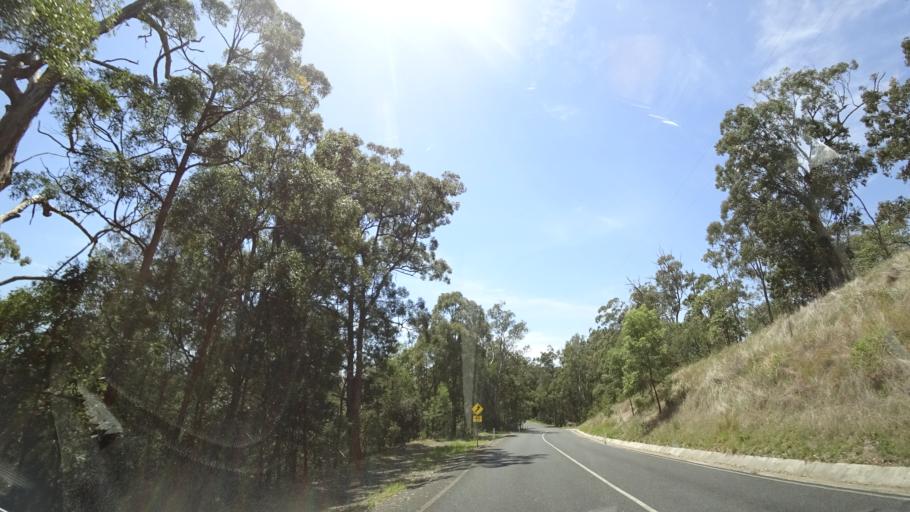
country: AU
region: Queensland
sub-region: Moreton Bay
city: Samford Valley
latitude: -27.4204
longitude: 152.8547
